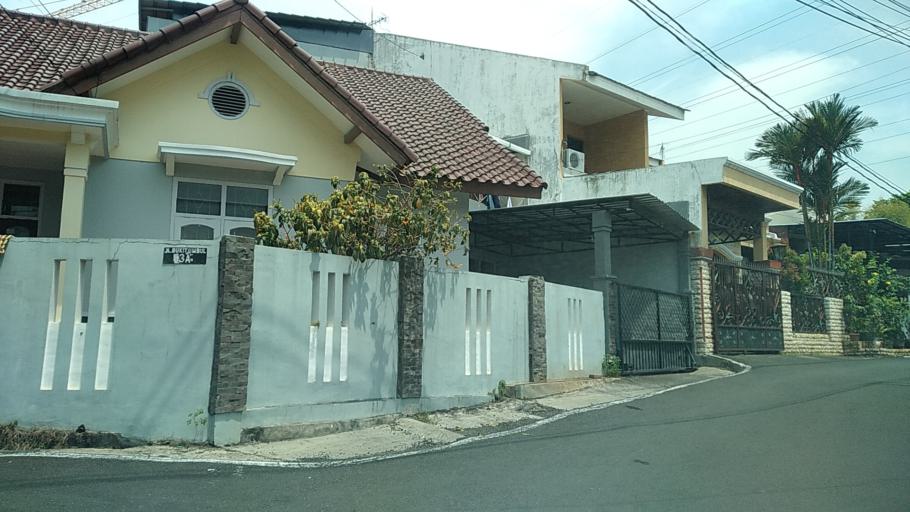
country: ID
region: Central Java
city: Semarang
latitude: -7.0508
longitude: 110.4287
